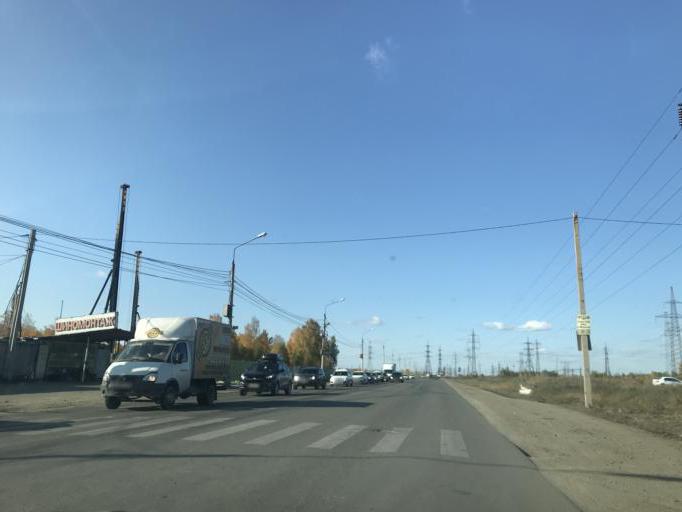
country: RU
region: Chelyabinsk
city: Roshchino
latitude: 55.2205
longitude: 61.2969
